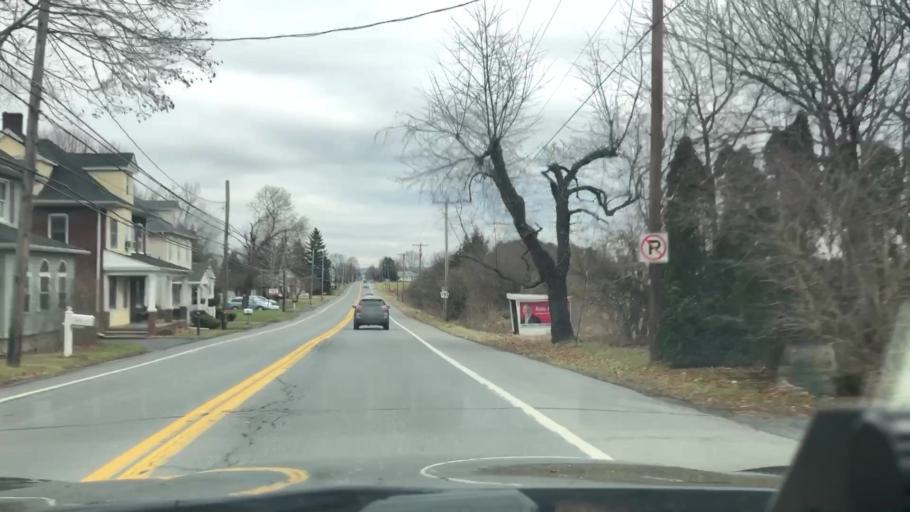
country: US
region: Pennsylvania
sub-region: Northampton County
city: Nazareth
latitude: 40.7052
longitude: -75.3289
